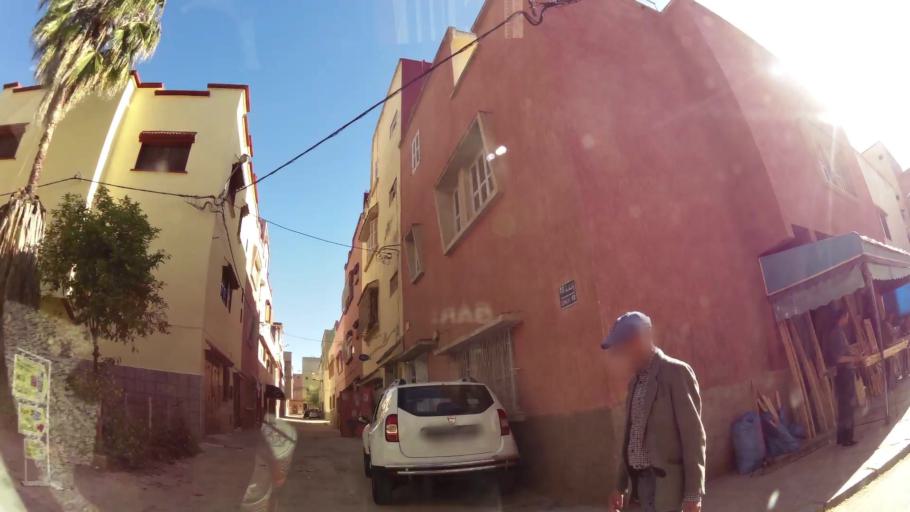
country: MA
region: Meknes-Tafilalet
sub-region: Meknes
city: Meknes
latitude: 33.8931
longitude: -5.5016
